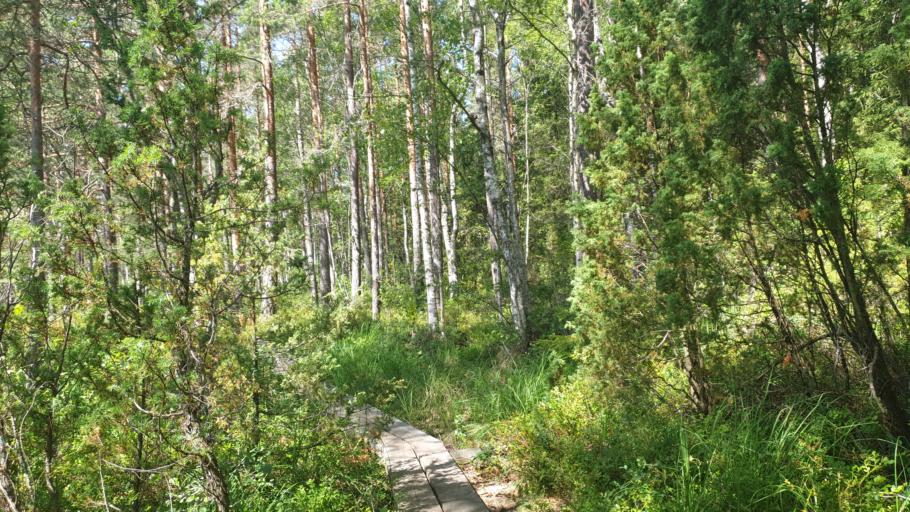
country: FI
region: Uusimaa
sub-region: Helsinki
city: Kirkkonummi
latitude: 60.3117
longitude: 24.4885
